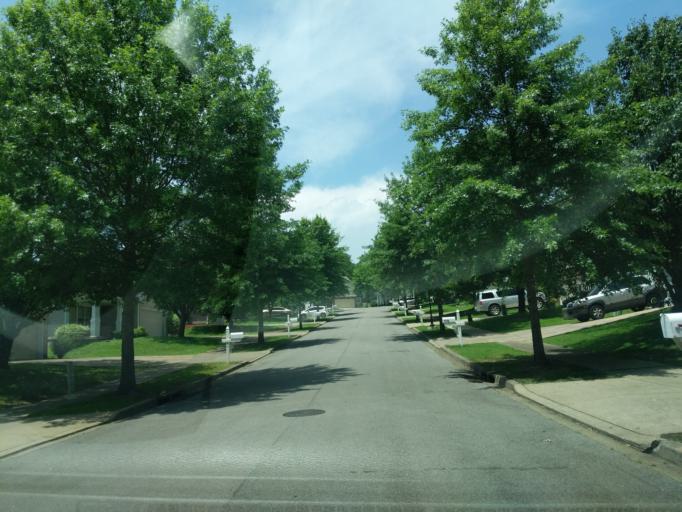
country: US
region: Tennessee
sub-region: Davidson County
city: Goodlettsville
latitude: 36.3007
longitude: -86.7251
